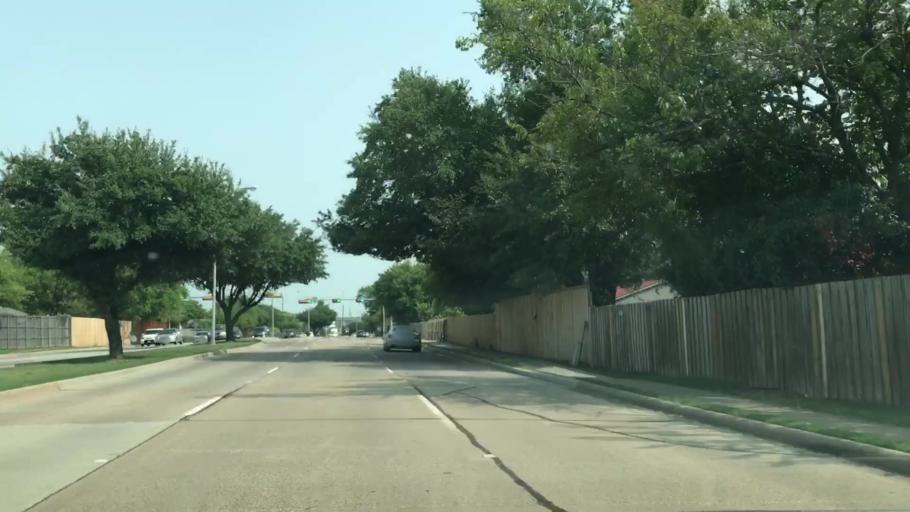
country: US
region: Texas
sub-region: Dallas County
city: Rowlett
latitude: 32.9165
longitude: -96.5724
